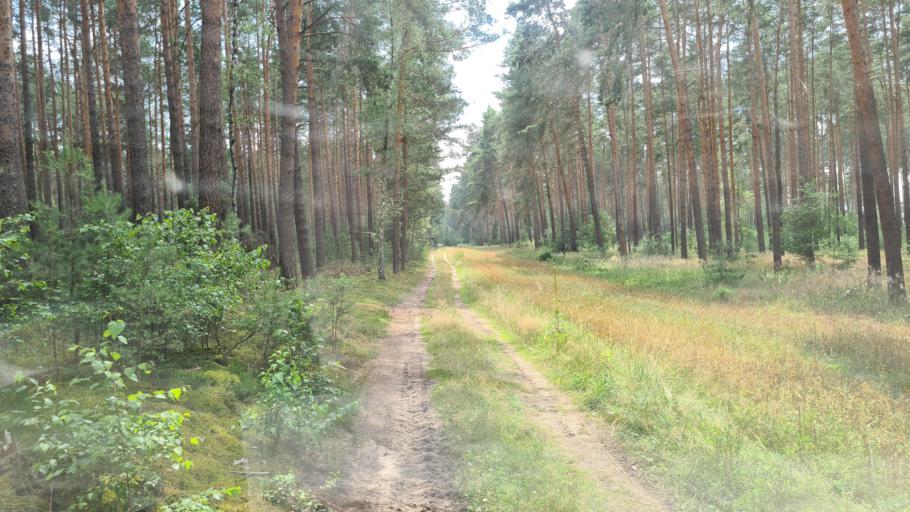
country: DE
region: Brandenburg
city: Bronkow
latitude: 51.7172
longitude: 13.8781
